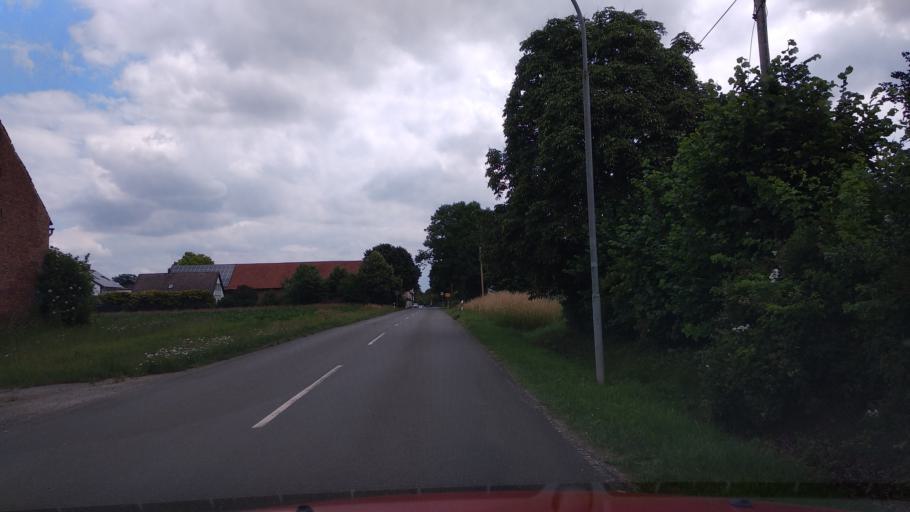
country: DE
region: North Rhine-Westphalia
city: Borgentreich
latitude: 51.5395
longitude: 9.1981
